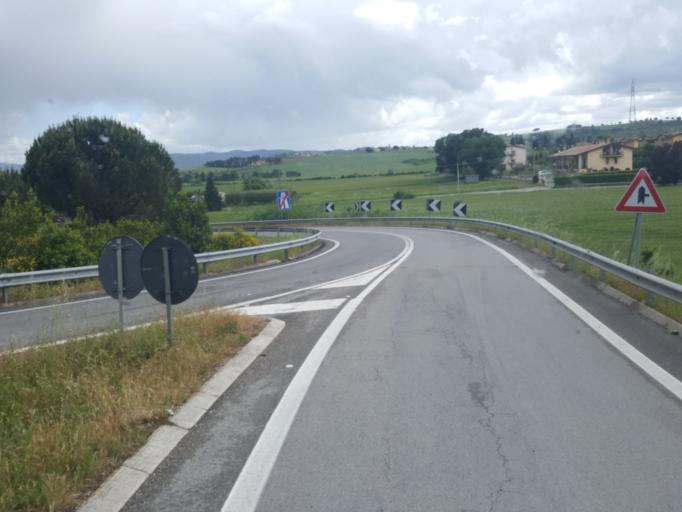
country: IT
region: Umbria
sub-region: Provincia di Perugia
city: Via Lippia
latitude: 43.0847
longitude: 12.4857
